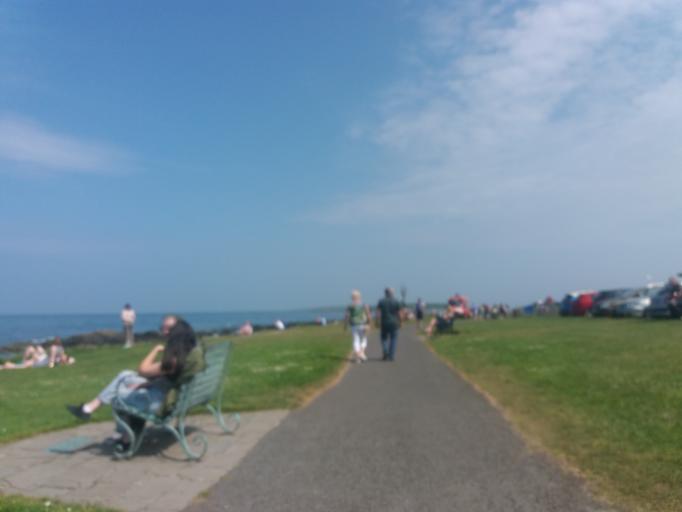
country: IE
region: Leinster
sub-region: Fingal County
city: Skerries
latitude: 53.5858
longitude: -6.1033
